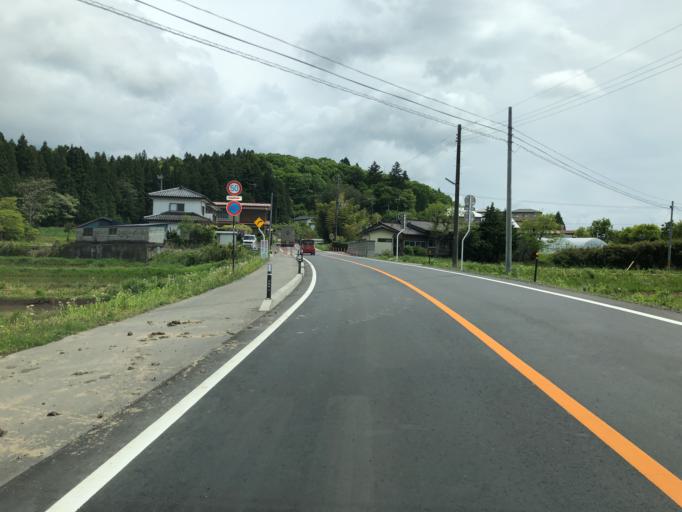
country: JP
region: Fukushima
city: Ishikawa
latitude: 37.0964
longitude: 140.3506
